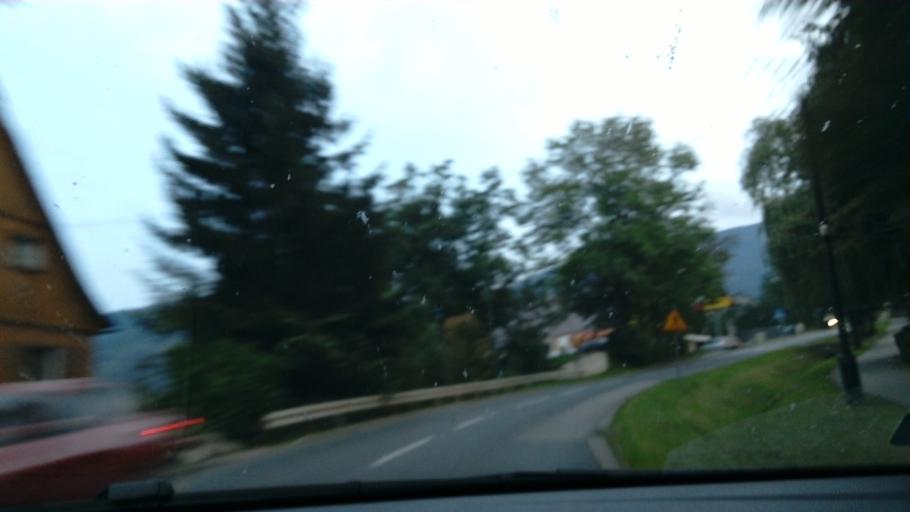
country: PL
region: Lower Silesian Voivodeship
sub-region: Powiat jeleniogorski
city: Karpacz
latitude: 50.7824
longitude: 15.7633
